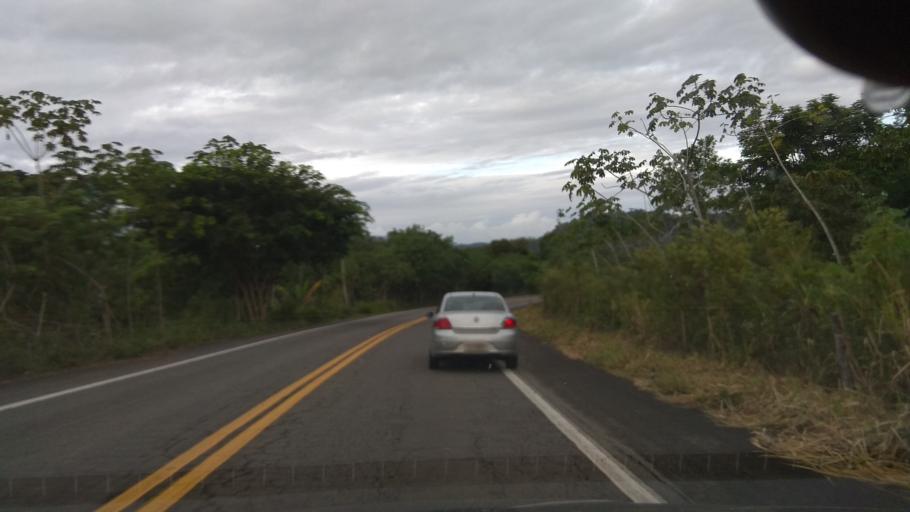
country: BR
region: Bahia
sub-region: Ubaitaba
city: Ubaitaba
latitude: -14.2620
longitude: -39.3351
